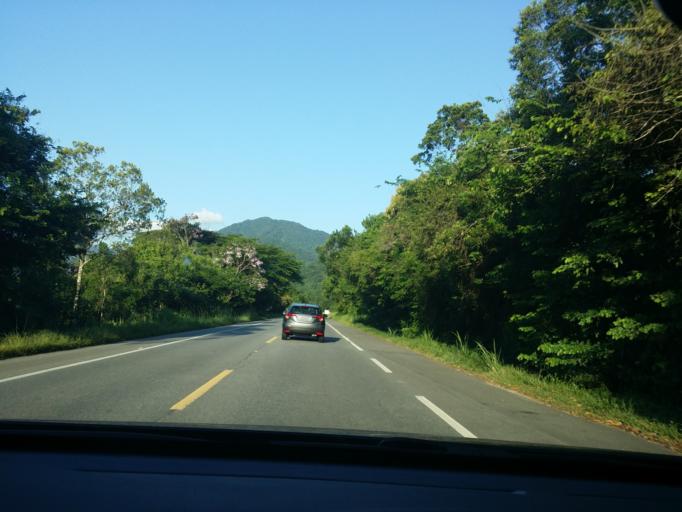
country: BR
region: Sao Paulo
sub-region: Biritiba-Mirim
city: Biritiba Mirim
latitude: -23.7510
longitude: -45.7495
